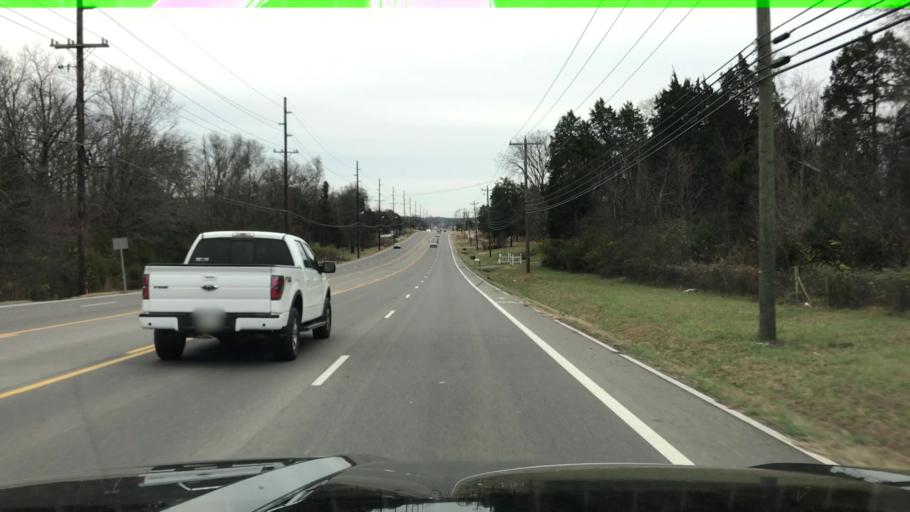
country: US
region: Tennessee
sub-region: Rutherford County
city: La Vergne
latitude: 36.0362
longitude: -86.5994
